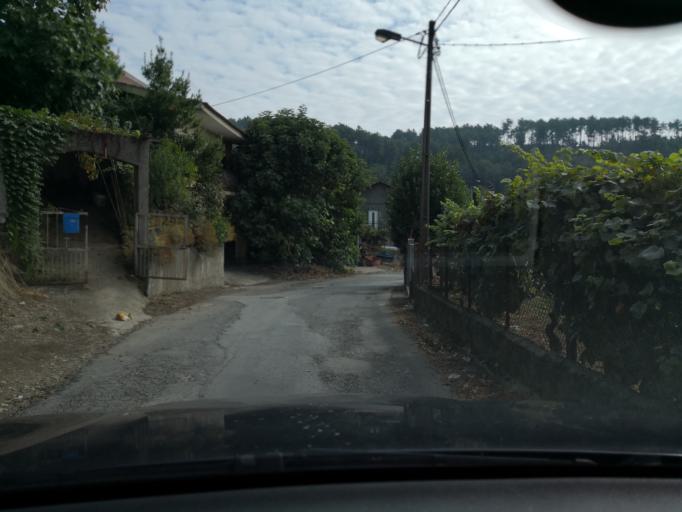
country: PT
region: Vila Real
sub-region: Sabrosa
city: Vilela
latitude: 41.2200
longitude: -7.6856
